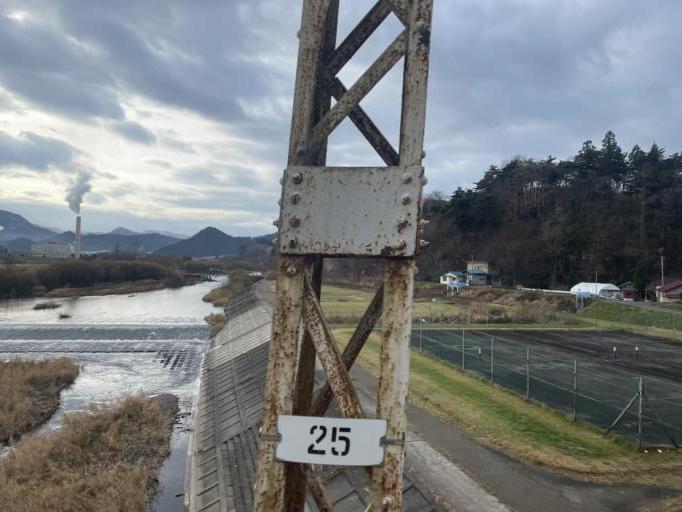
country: JP
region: Aomori
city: Hirosaki
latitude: 40.5494
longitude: 140.5467
